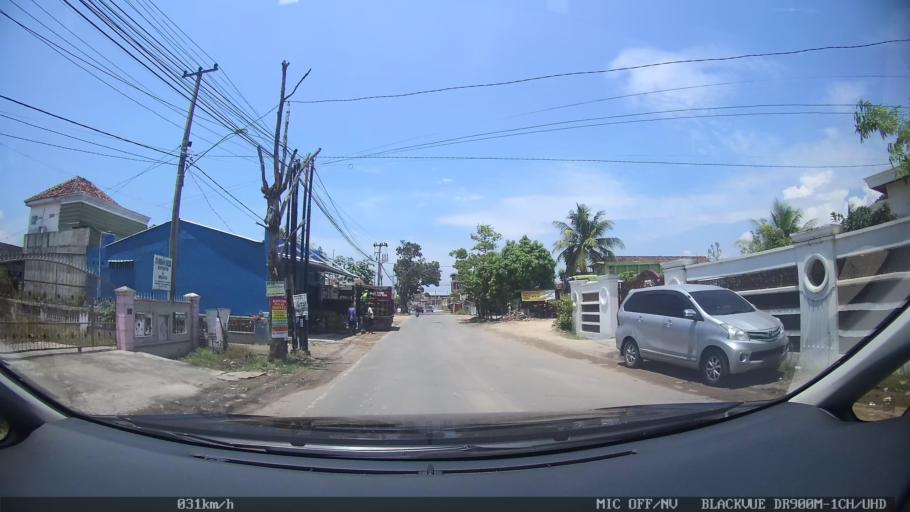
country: ID
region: Lampung
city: Kedaton
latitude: -5.3719
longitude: 105.2893
